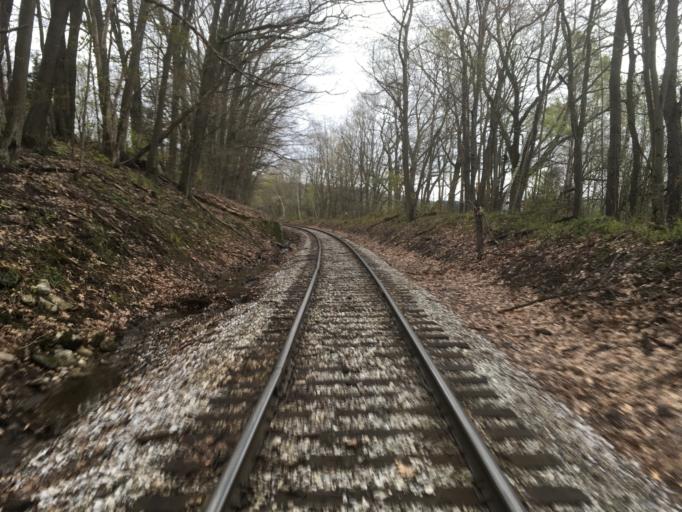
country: US
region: Vermont
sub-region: Rutland County
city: Rutland
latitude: 43.4803
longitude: -72.8759
